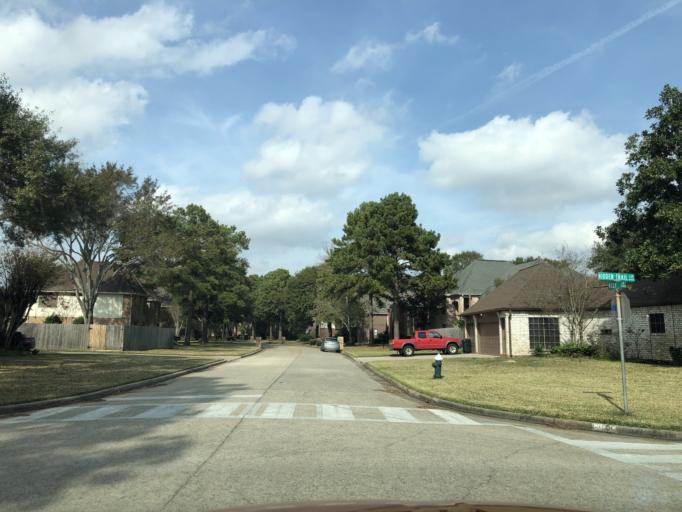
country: US
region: Texas
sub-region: Harris County
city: Tomball
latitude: 30.0221
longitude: -95.5444
